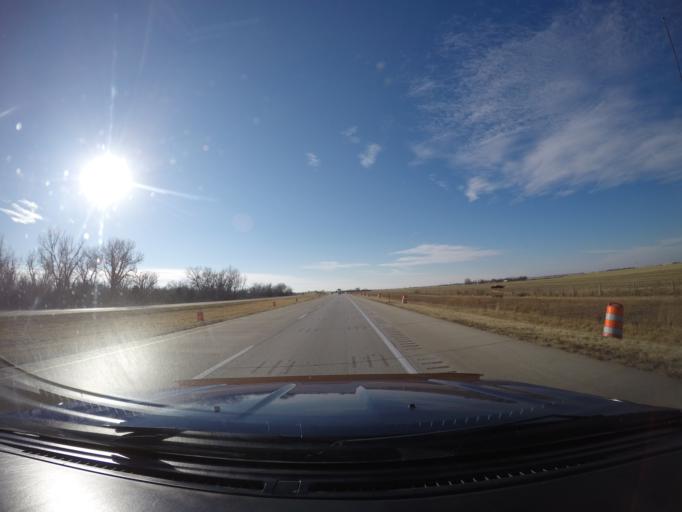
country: US
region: Nebraska
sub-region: Buffalo County
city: Kearney
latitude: 40.6812
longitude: -98.9826
